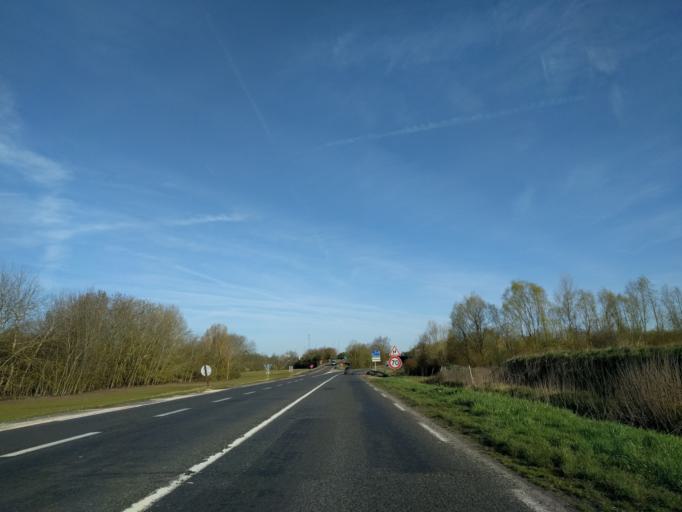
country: FR
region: Ile-de-France
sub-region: Departement de Seine-et-Marne
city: Moissy-Cramayel
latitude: 48.6052
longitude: 2.5831
